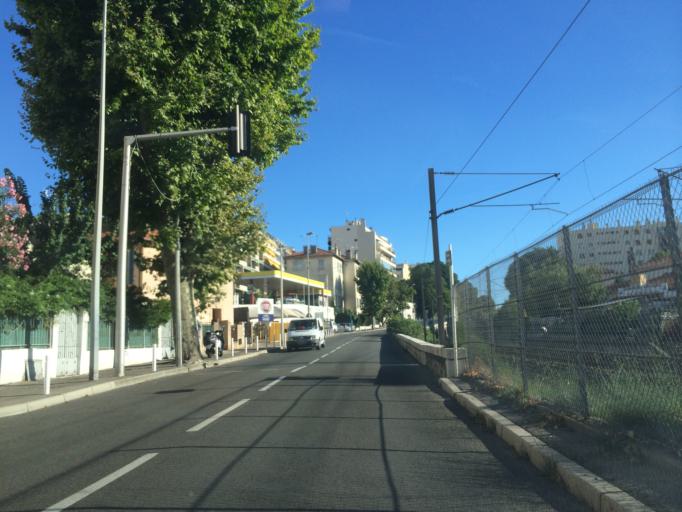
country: FR
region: Provence-Alpes-Cote d'Azur
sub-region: Departement des Alpes-Maritimes
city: Antibes
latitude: 43.5773
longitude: 7.1174
